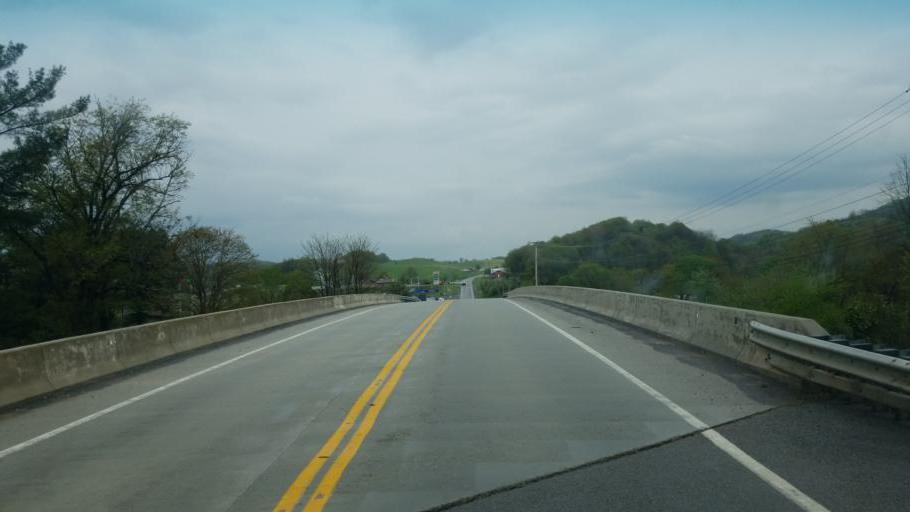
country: US
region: Virginia
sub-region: Smyth County
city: Atkins
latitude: 36.8843
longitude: -81.3763
